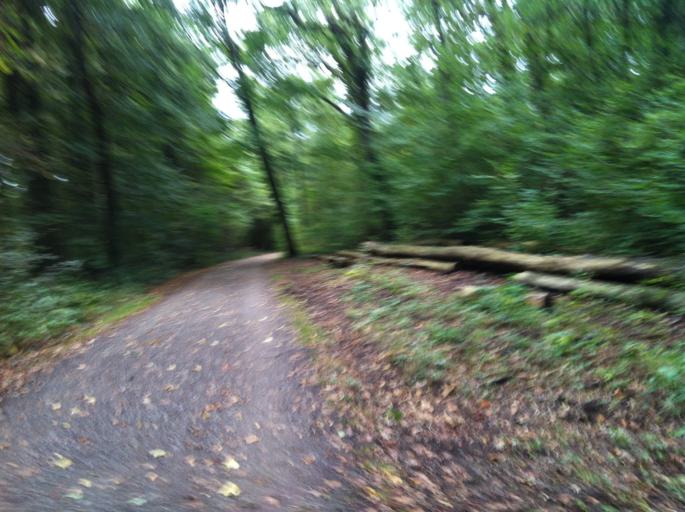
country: DE
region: Rheinland-Pfalz
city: Budenheim
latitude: 50.0143
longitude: 8.1752
